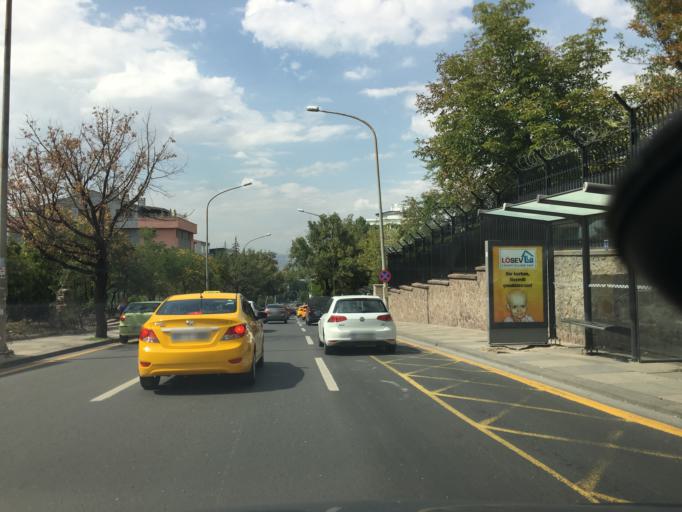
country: TR
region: Ankara
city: Cankaya
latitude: 39.8976
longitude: 32.8615
